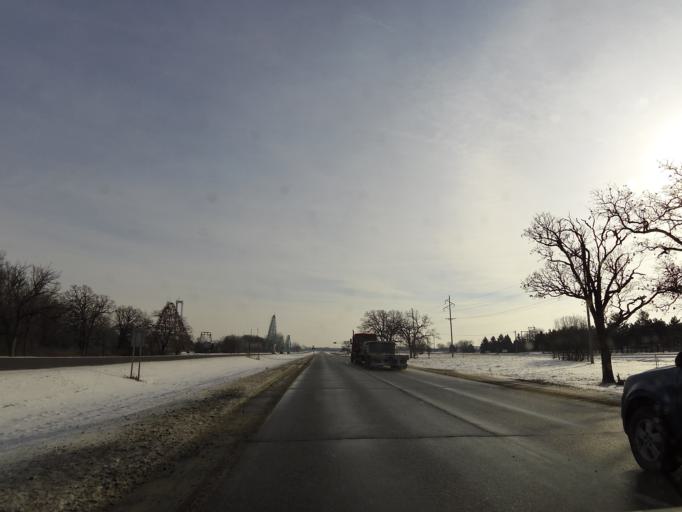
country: US
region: Minnesota
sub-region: Hennepin County
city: Eden Prairie
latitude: 44.7994
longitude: -93.4669
